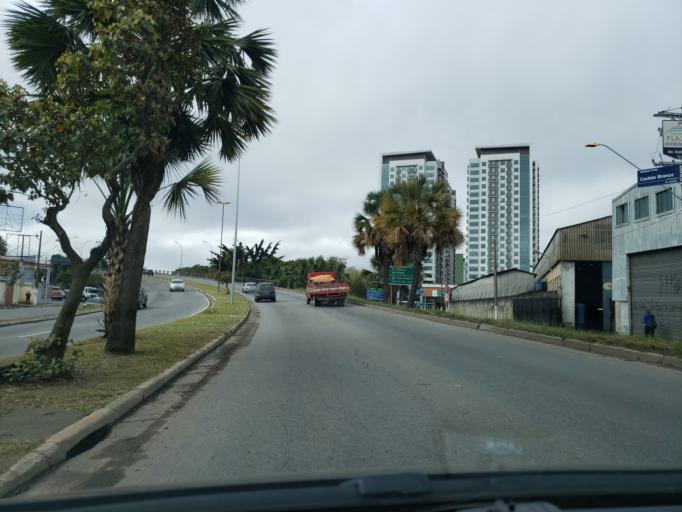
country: BR
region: Sao Paulo
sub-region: Santo Andre
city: Santo Andre
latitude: -23.6430
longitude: -46.5392
